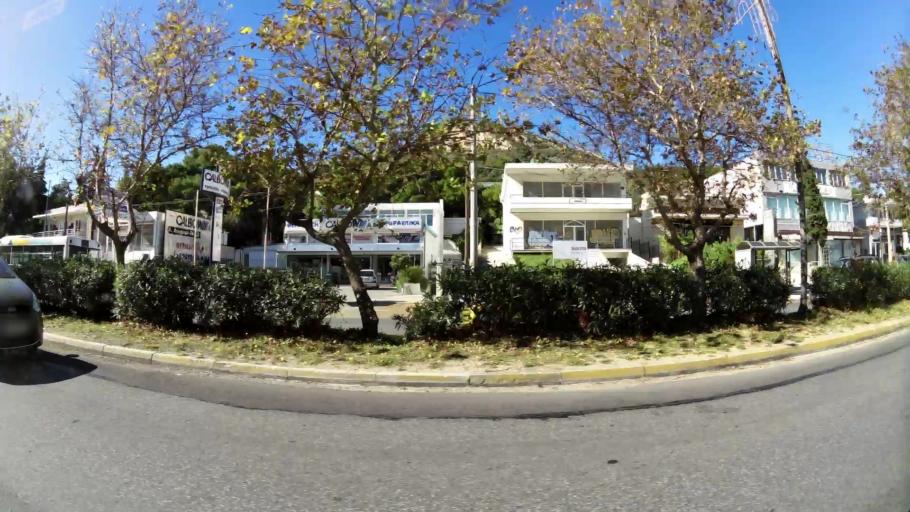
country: GR
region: Attica
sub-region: Nomarchia Anatolikis Attikis
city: Leondarion
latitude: 38.0035
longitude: 23.8476
